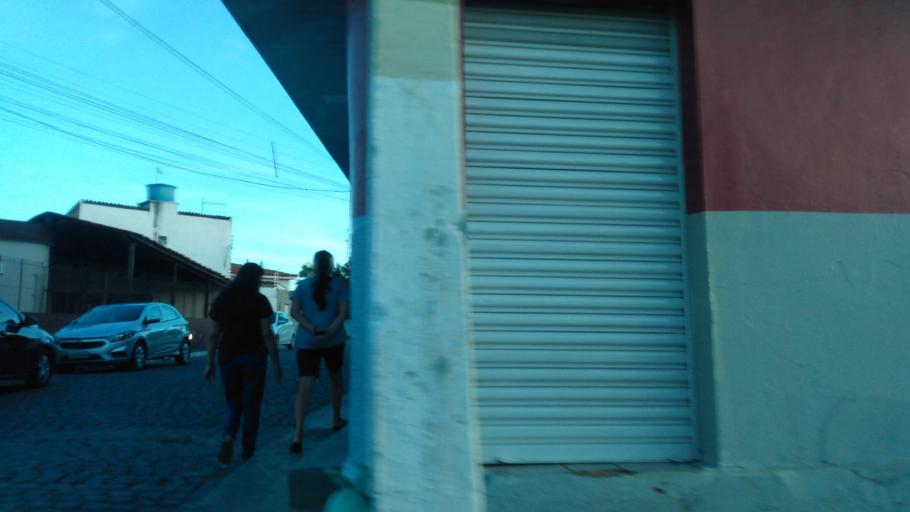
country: BR
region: Pernambuco
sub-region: Bezerros
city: Bezerros
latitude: -8.2409
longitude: -35.7532
